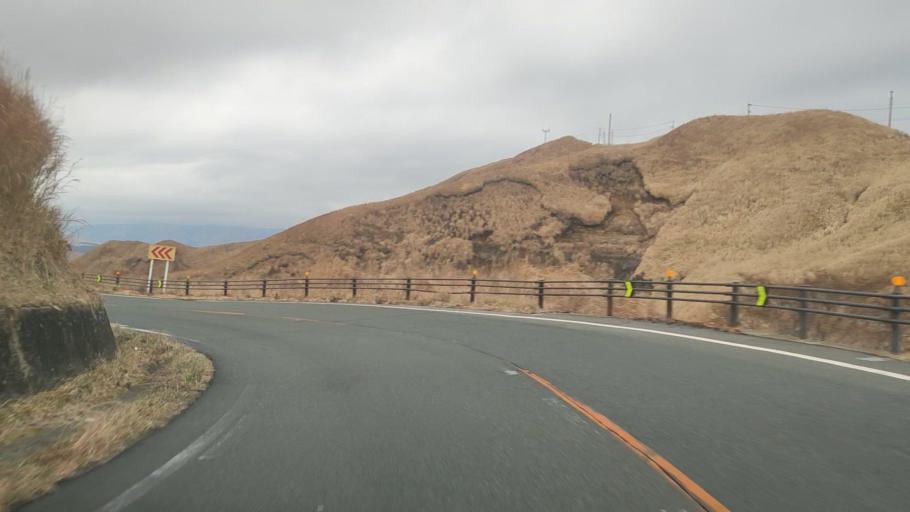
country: JP
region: Kumamoto
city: Aso
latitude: 32.9053
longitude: 131.1534
